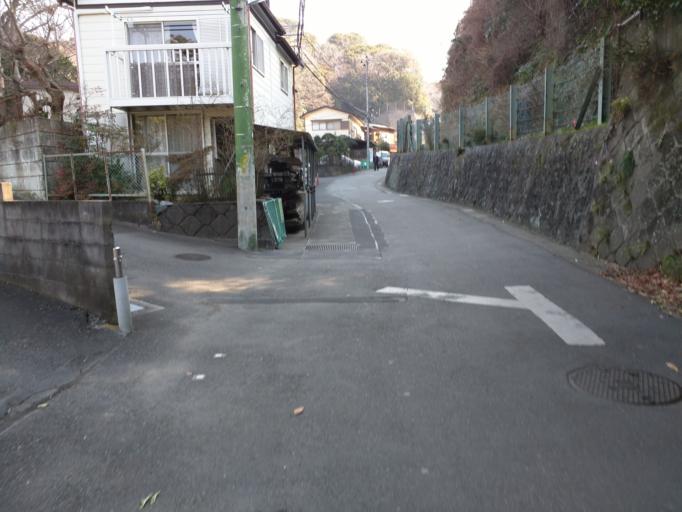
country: JP
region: Kanagawa
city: Kamakura
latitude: 35.3273
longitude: 139.5700
